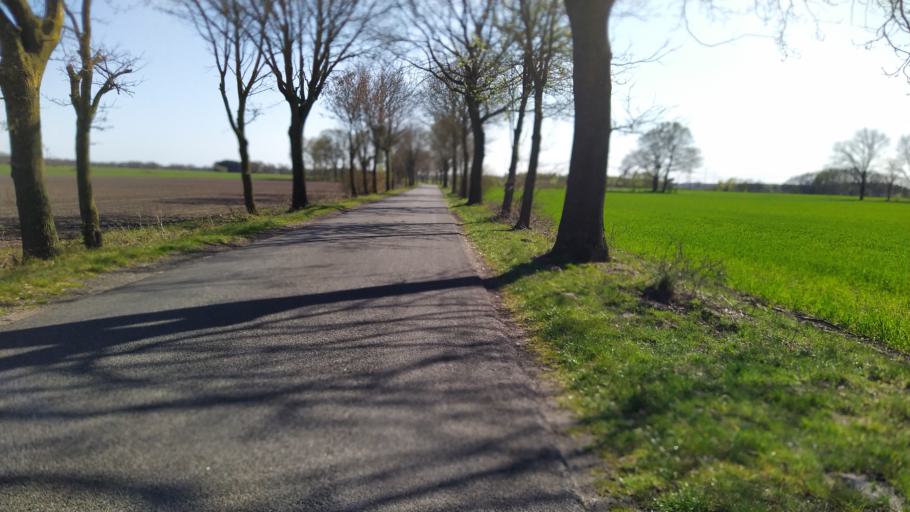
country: DE
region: Lower Saxony
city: Heeslingen
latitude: 53.3205
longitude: 9.3896
